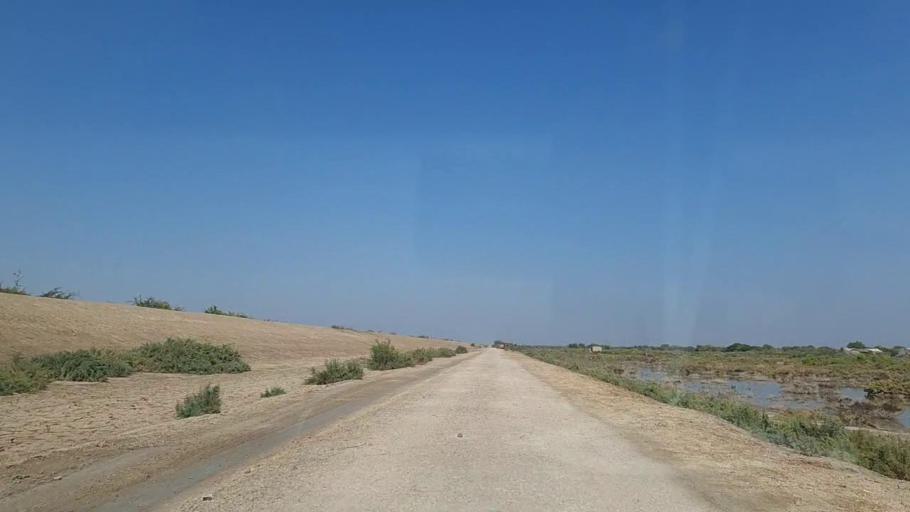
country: PK
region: Sindh
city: Chuhar Jamali
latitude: 24.4573
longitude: 68.0007
